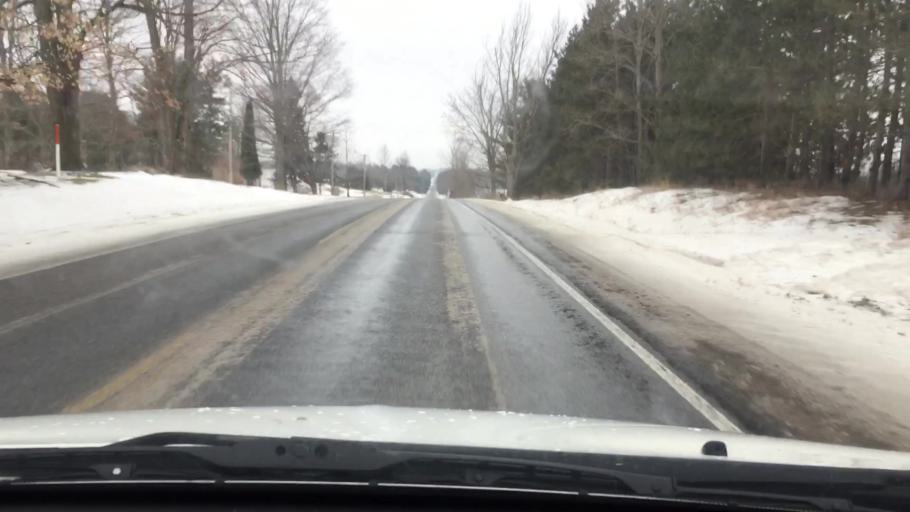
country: US
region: Michigan
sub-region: Wexford County
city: Cadillac
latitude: 44.0667
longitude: -85.4440
